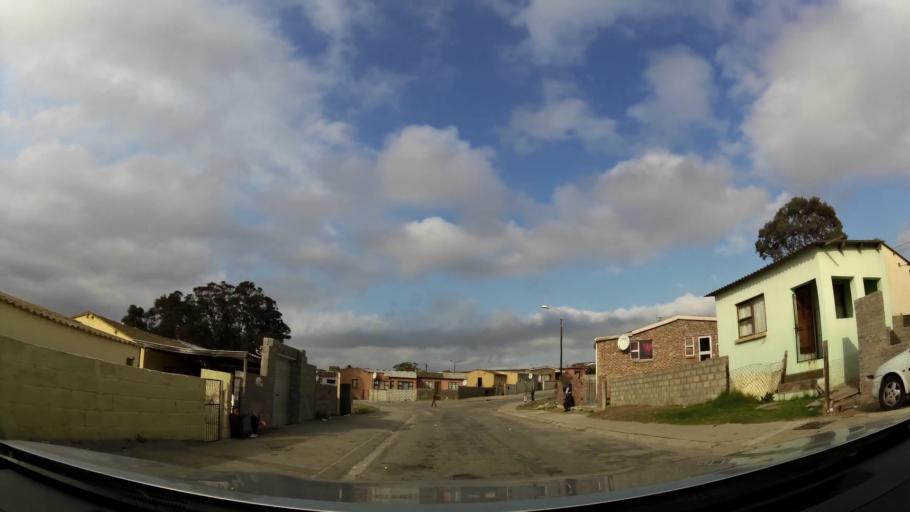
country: ZA
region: Eastern Cape
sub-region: Nelson Mandela Bay Metropolitan Municipality
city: Port Elizabeth
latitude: -33.9146
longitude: 25.5455
